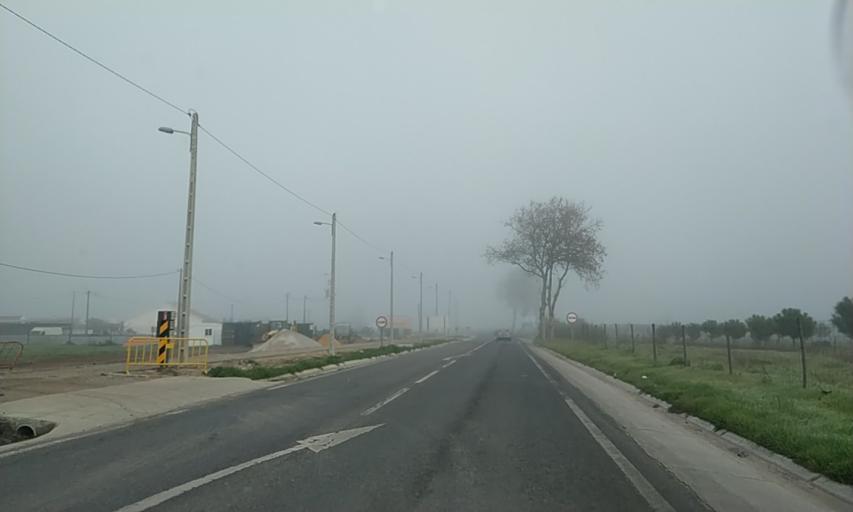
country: PT
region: Setubal
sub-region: Palmela
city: Pinhal Novo
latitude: 38.6450
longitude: -8.9149
